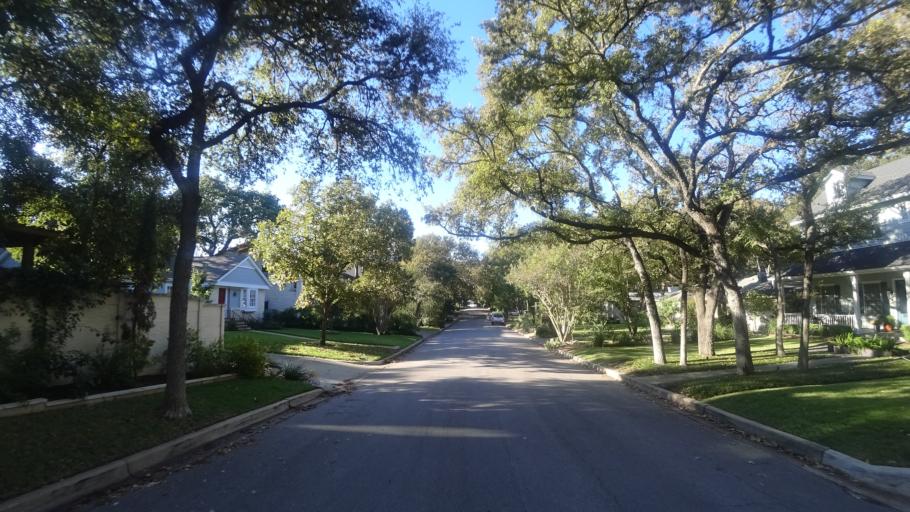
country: US
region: Texas
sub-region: Travis County
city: Rollingwood
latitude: 30.2963
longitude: -97.7721
